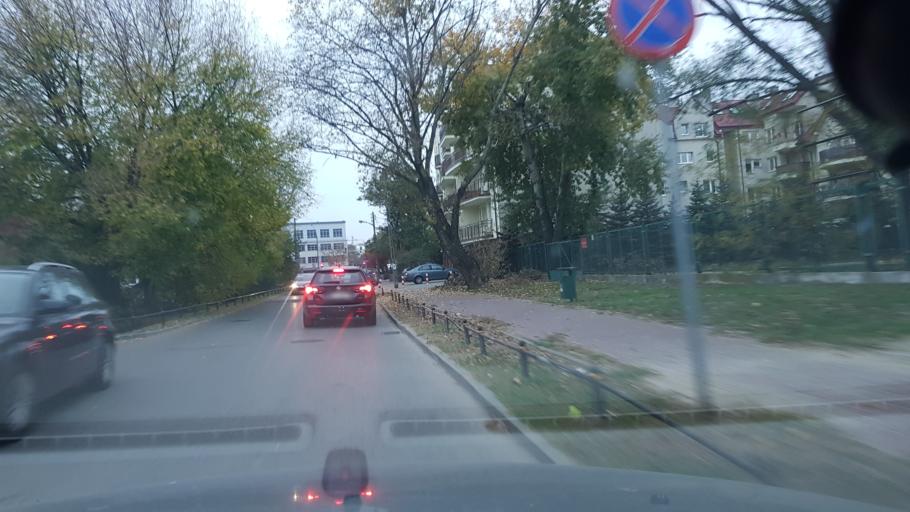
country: PL
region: Masovian Voivodeship
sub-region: Warszawa
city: Ursynow
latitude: 52.1472
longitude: 21.0202
